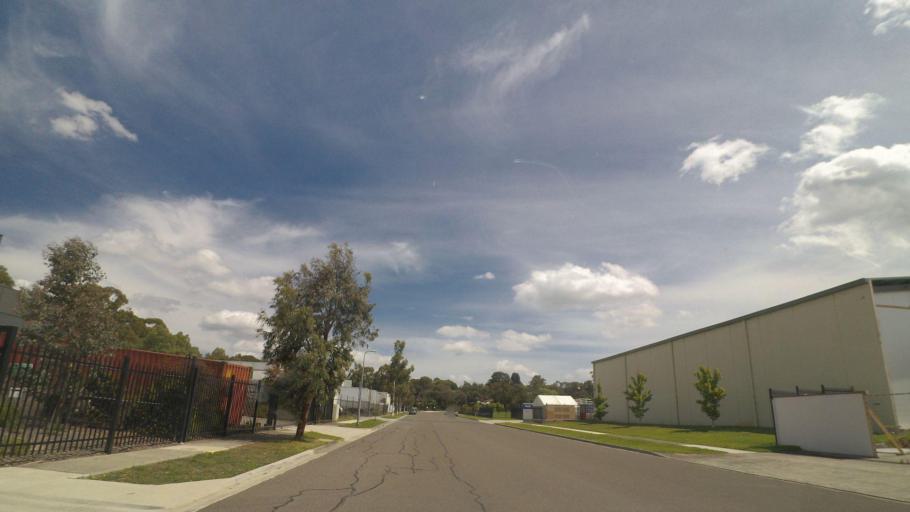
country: AU
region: Victoria
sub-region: Maroondah
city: Bayswater North
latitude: -37.8381
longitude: 145.2963
